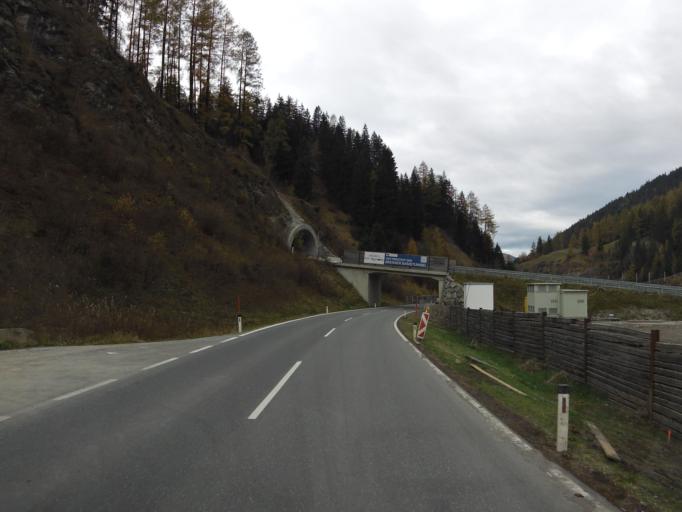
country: AT
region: Tyrol
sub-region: Politischer Bezirk Innsbruck Land
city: Steinach am Brenner
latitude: 47.0750
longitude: 11.4825
